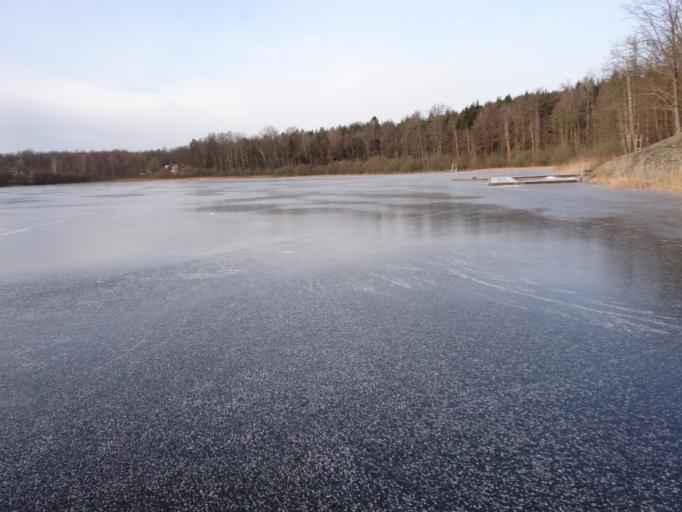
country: SE
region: Blekinge
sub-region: Karlshamns Kommun
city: Karlshamn
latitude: 56.2180
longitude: 14.9630
